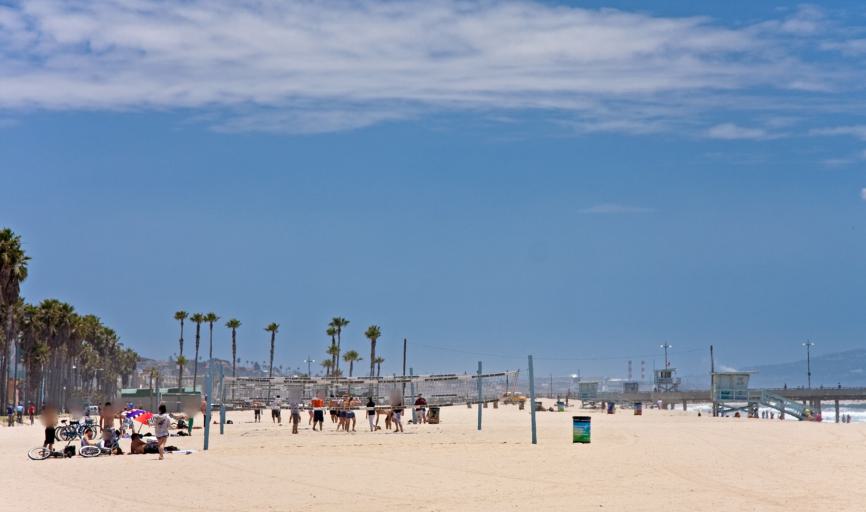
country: US
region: California
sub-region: Los Angeles County
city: Marina del Rey
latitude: 33.9830
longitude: -118.4708
